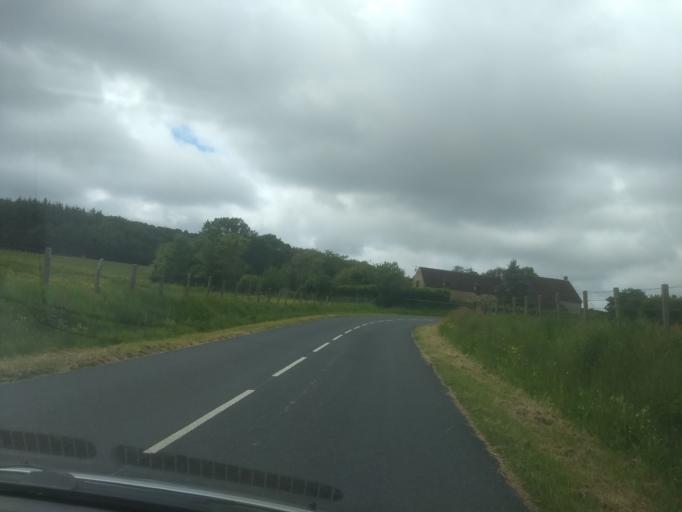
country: FR
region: Lower Normandy
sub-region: Departement de l'Orne
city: Bretoncelles
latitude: 48.4733
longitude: 0.8433
